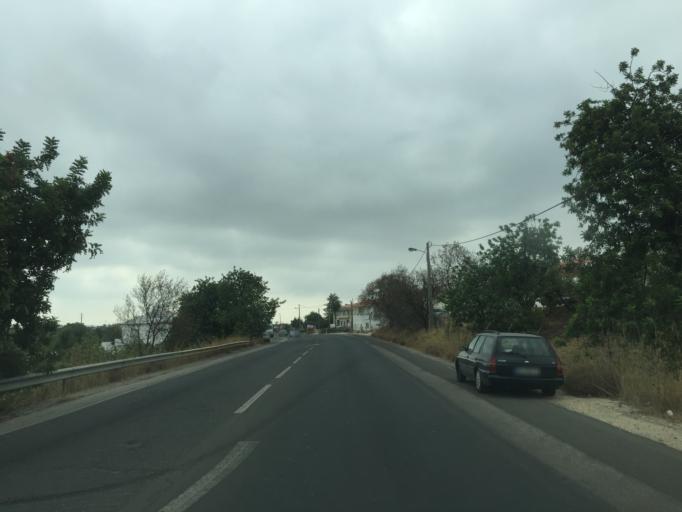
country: PT
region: Faro
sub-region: Faro
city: Santa Barbara de Nexe
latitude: 37.0758
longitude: -7.9839
